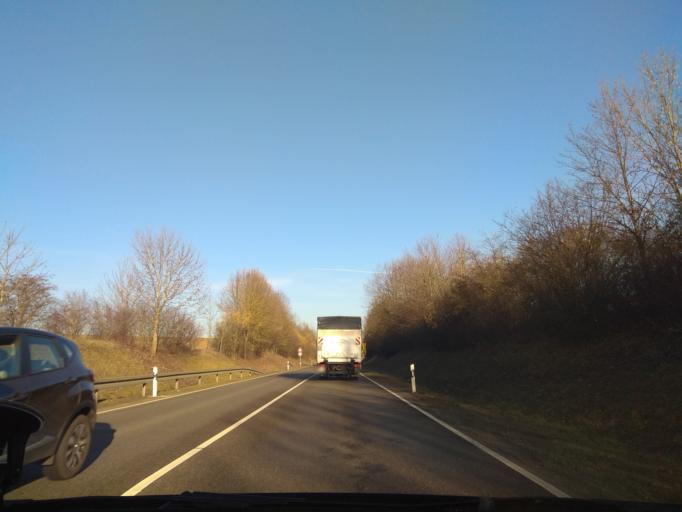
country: DE
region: Baden-Wuerttemberg
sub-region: Tuebingen Region
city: Sickenhausen
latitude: 48.5407
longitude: 9.1815
